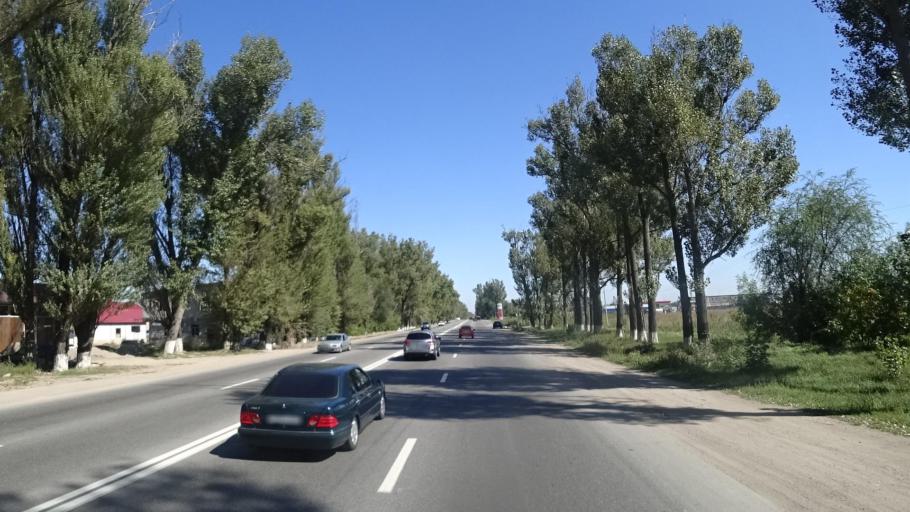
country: KZ
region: Almaty Oblysy
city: Energeticheskiy
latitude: 43.3580
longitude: 77.0740
